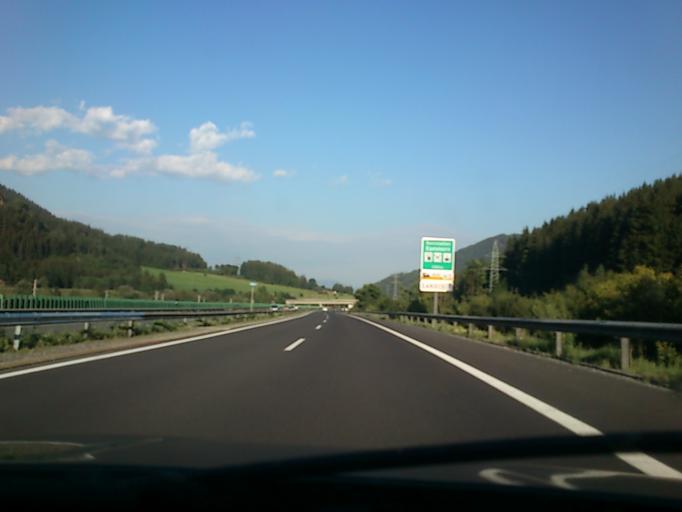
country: AT
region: Styria
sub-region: Politischer Bezirk Leoben
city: Kammern im Liesingtal
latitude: 47.3918
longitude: 14.8708
